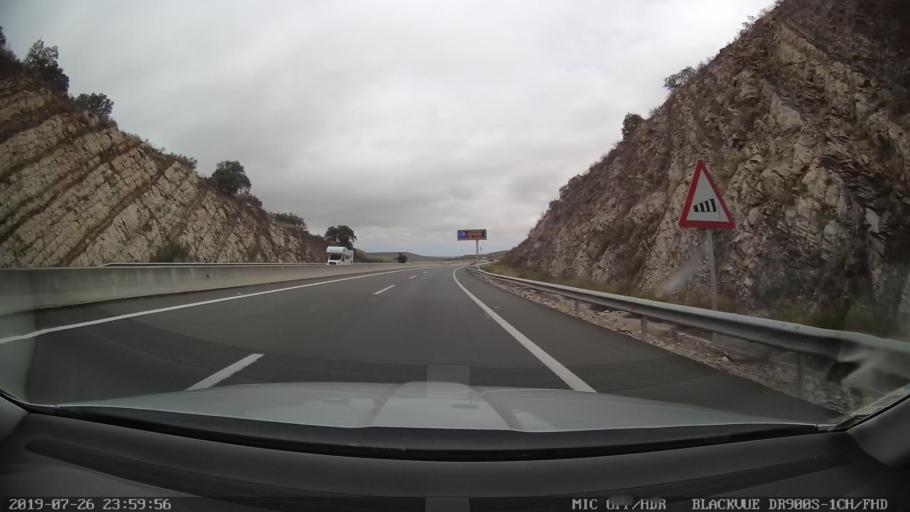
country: ES
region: Extremadura
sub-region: Provincia de Caceres
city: Romangordo
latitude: 39.7765
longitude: -5.7357
